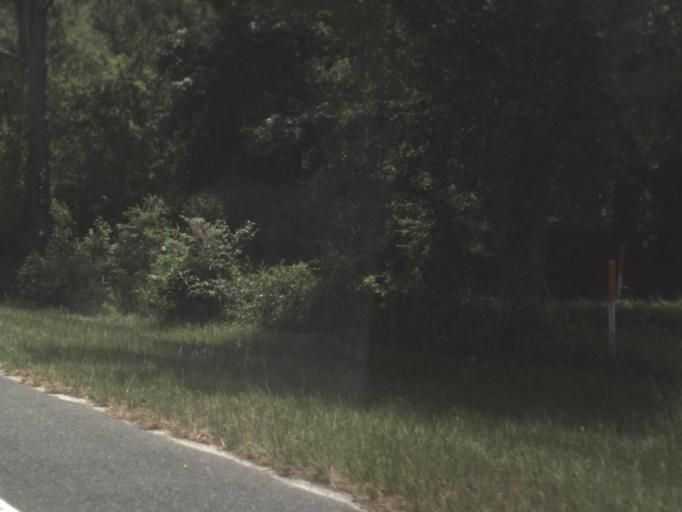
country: US
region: Florida
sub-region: Union County
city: Lake Butler
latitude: 30.0038
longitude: -82.4963
